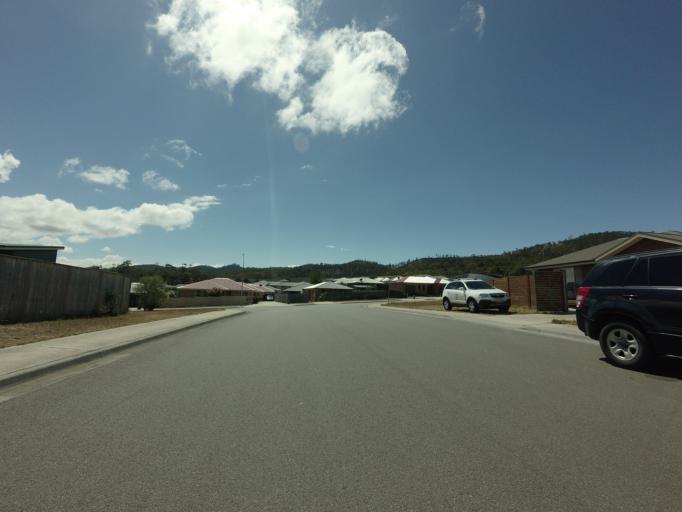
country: AU
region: Tasmania
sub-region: Clarence
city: Rokeby
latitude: -42.8996
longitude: 147.4524
